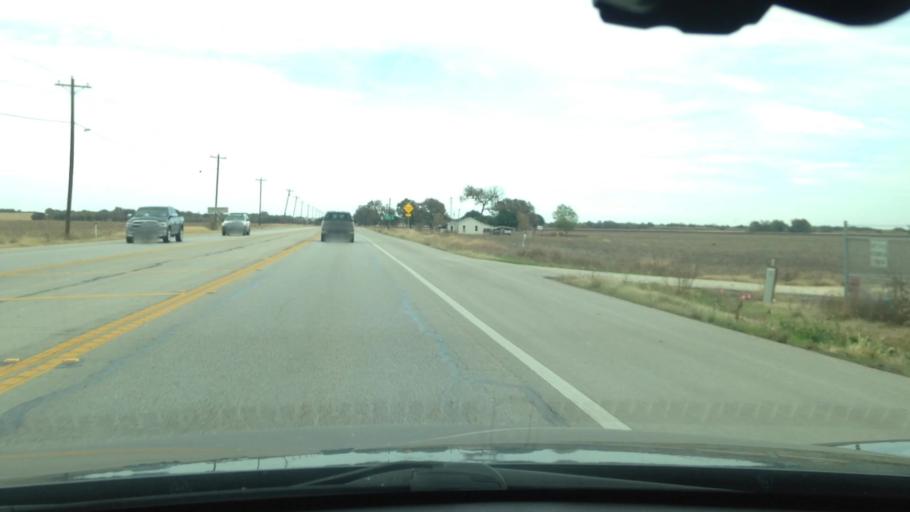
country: US
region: Texas
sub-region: Caldwell County
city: Uhland
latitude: 29.9235
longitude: -97.8347
